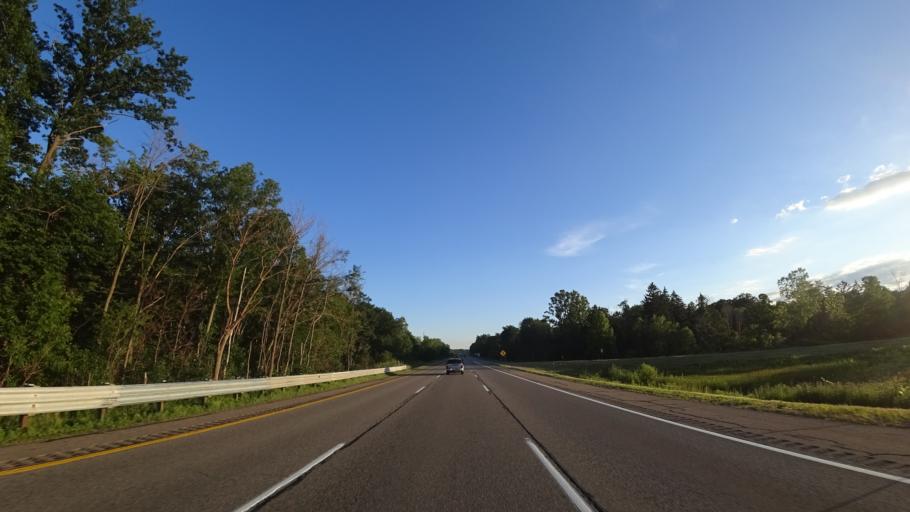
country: US
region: Michigan
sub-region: Berrien County
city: New Buffalo
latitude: 41.7975
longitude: -86.7095
